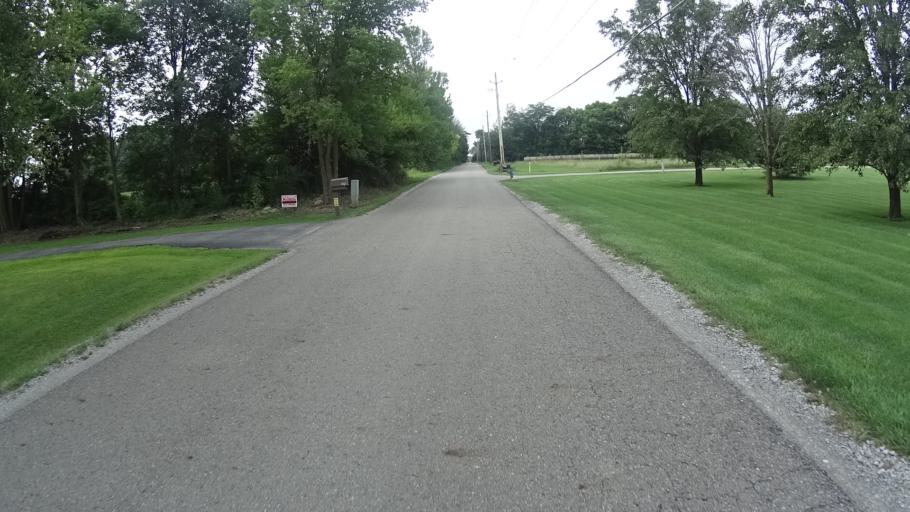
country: US
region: Indiana
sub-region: Madison County
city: Pendleton
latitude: 40.0074
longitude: -85.7870
